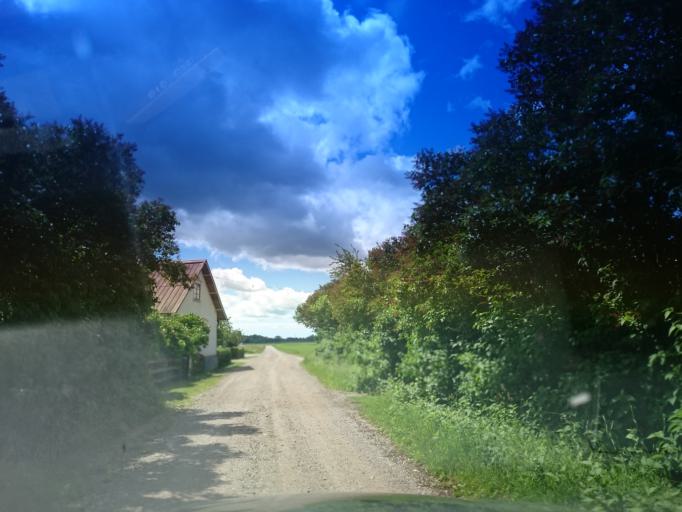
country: SE
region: Gotland
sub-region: Gotland
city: Hemse
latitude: 57.3456
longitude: 18.6408
